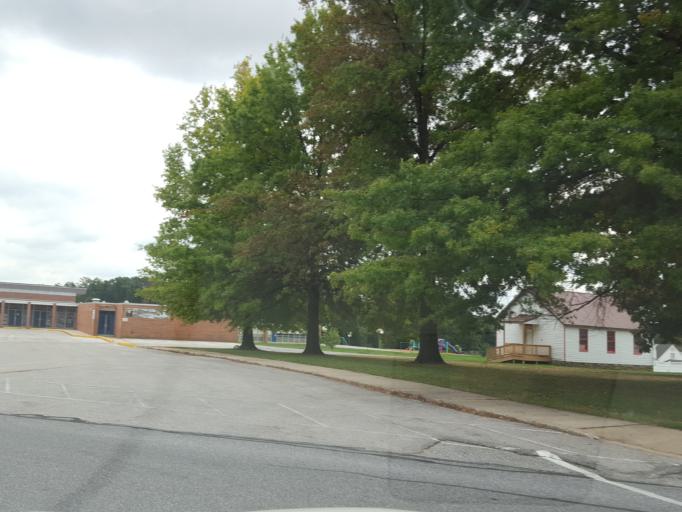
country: US
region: Pennsylvania
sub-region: York County
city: Red Lion
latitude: 39.8938
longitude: -76.6090
